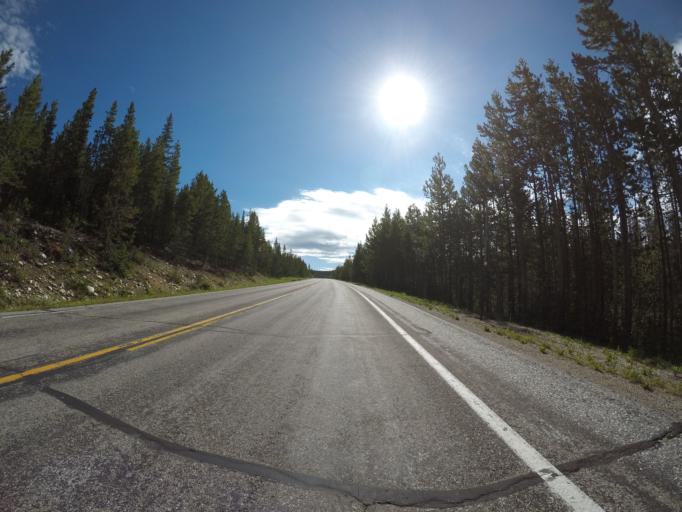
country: US
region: Wyoming
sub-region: Carbon County
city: Saratoga
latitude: 41.3229
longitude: -106.4551
